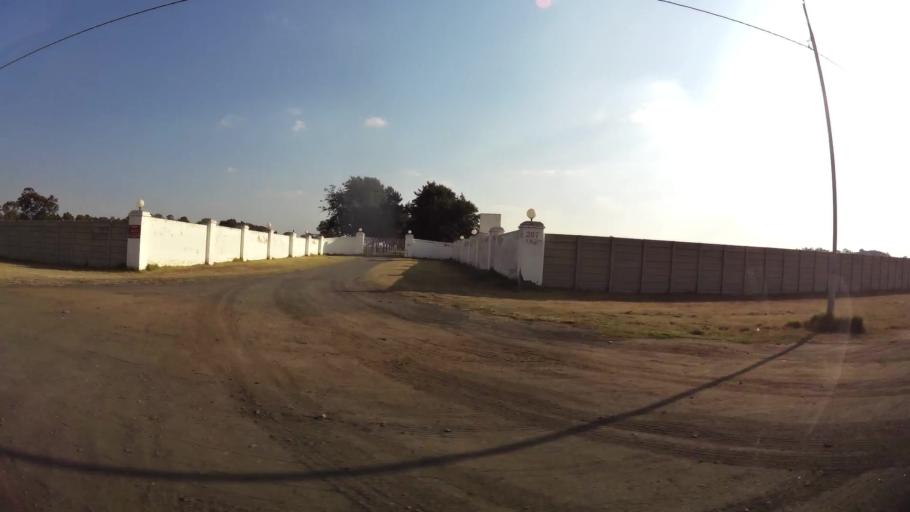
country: ZA
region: Gauteng
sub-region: Ekurhuleni Metropolitan Municipality
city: Benoni
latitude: -26.1162
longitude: 28.3894
